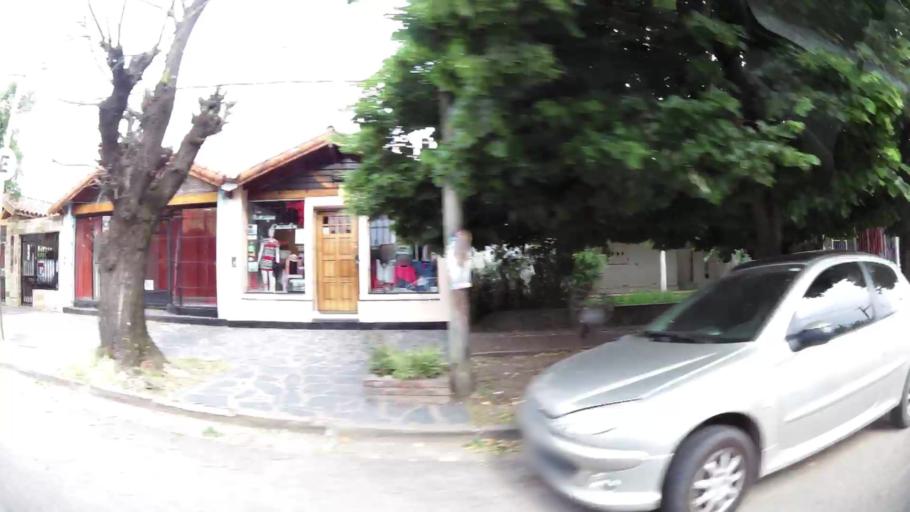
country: AR
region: Buenos Aires
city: San Justo
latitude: -34.7265
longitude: -58.5336
